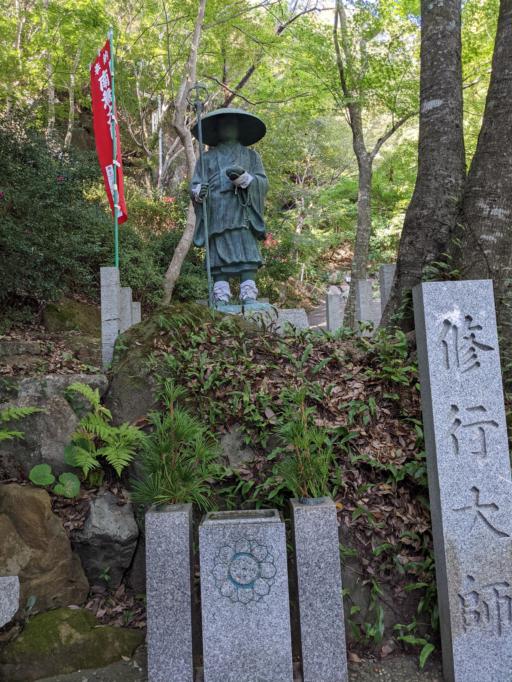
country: JP
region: Wakayama
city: Tanabe
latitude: 33.7145
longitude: 135.4282
